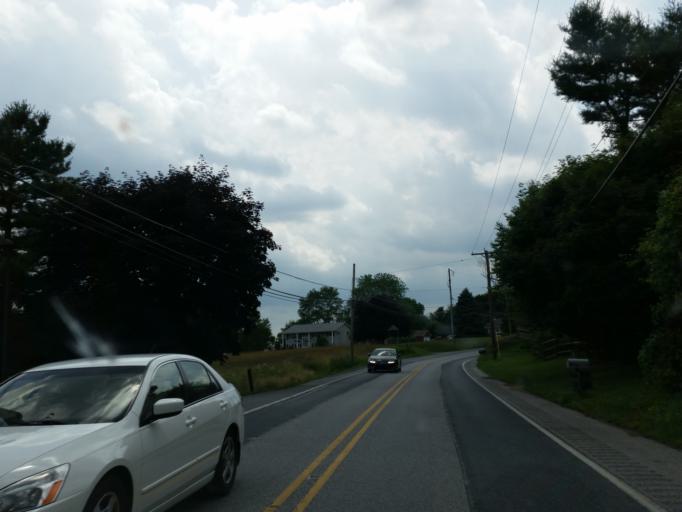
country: US
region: Pennsylvania
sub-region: Chester County
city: West Grove
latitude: 39.7476
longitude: -75.8164
